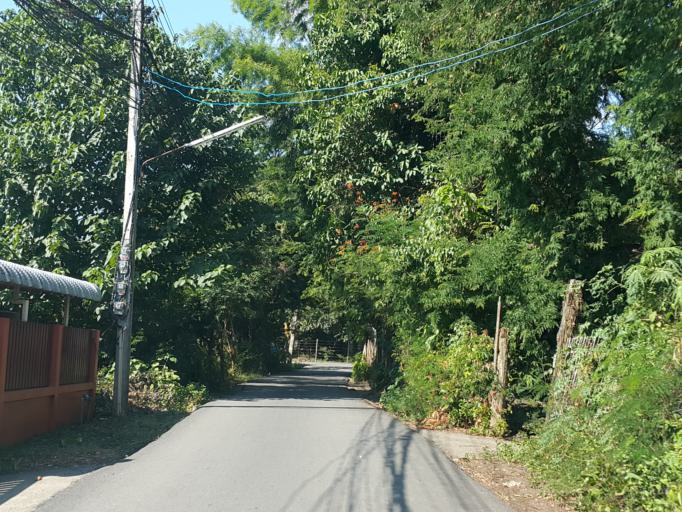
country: TH
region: Chiang Mai
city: San Sai
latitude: 18.9108
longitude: 98.9392
